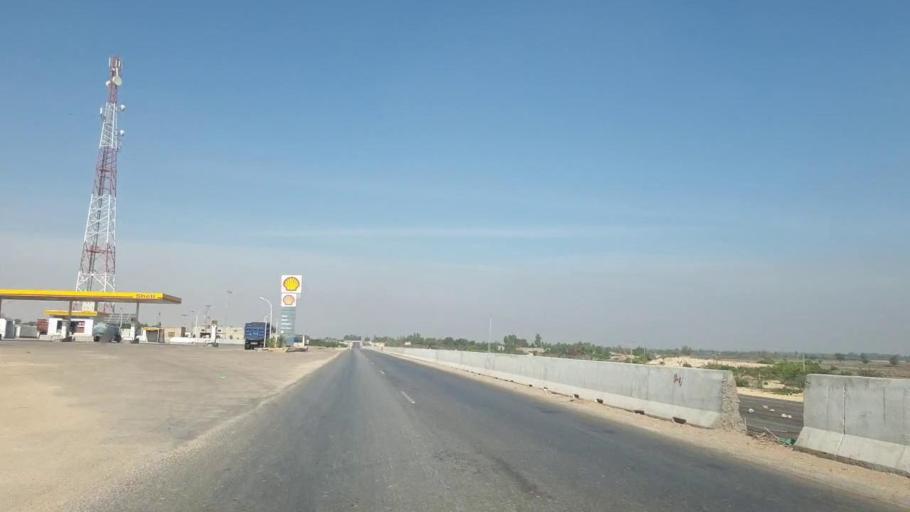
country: PK
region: Sindh
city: Hala
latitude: 25.7044
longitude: 68.2957
